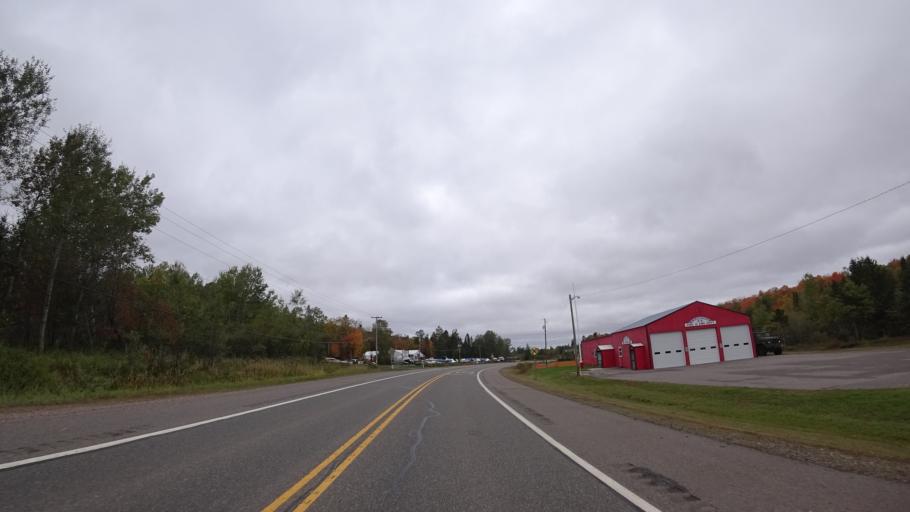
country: US
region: Michigan
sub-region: Marquette County
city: West Ishpeming
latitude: 46.5147
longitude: -87.9698
